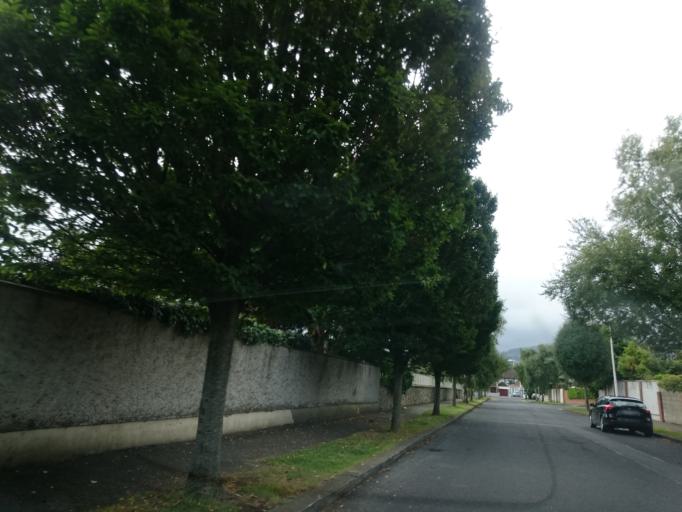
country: IE
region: Leinster
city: Mount Merrion
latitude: 53.2902
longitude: -6.2185
